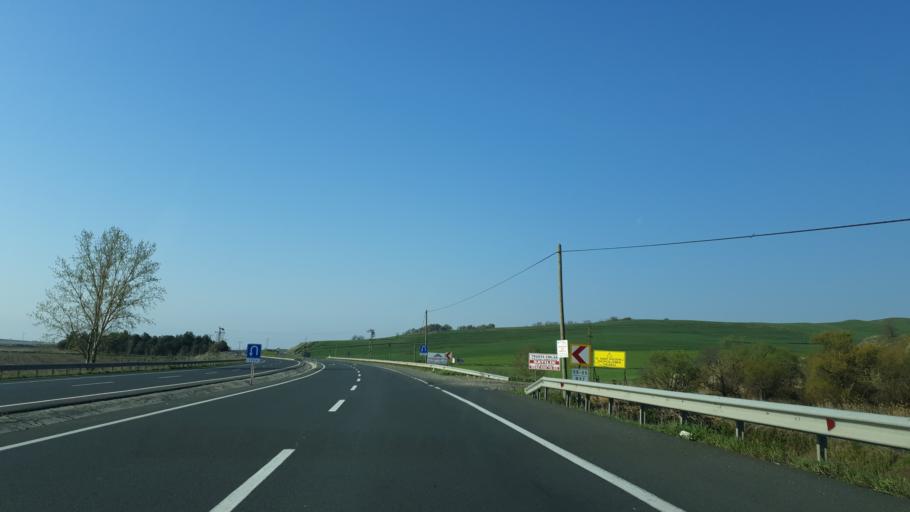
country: TR
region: Tekirdag
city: Corlu
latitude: 41.0501
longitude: 27.7347
